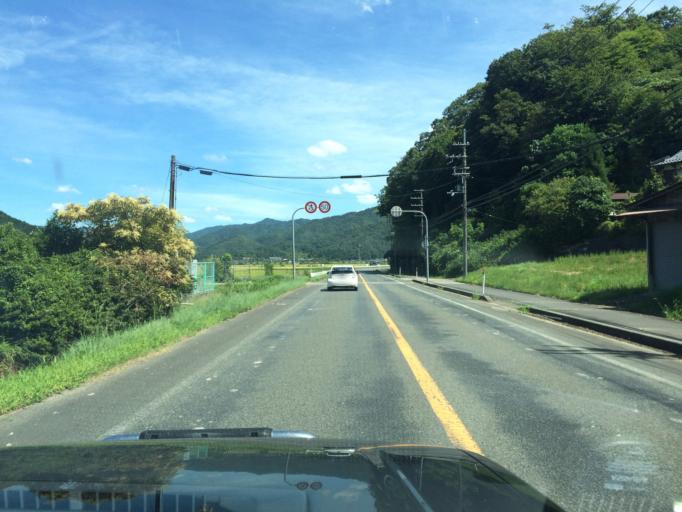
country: JP
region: Hyogo
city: Toyooka
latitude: 35.4672
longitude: 134.8513
